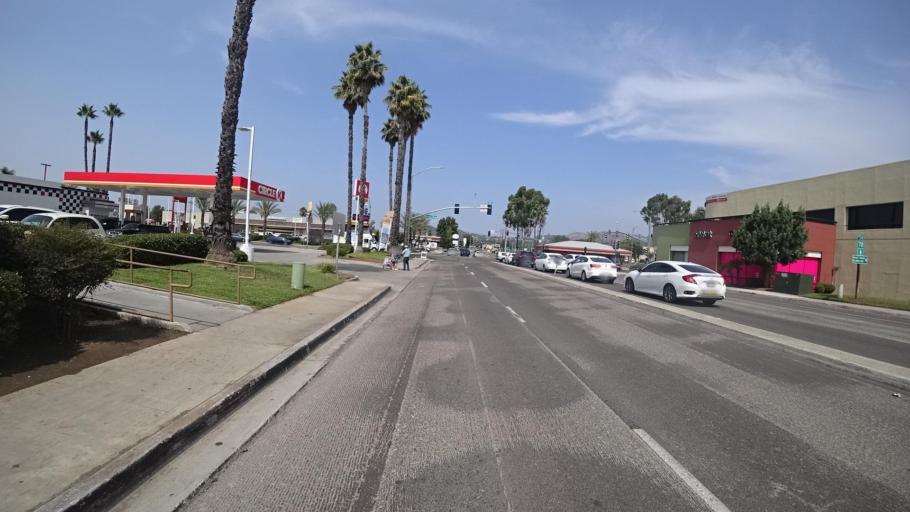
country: US
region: California
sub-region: San Diego County
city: Escondido
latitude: 33.1300
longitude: -117.0669
